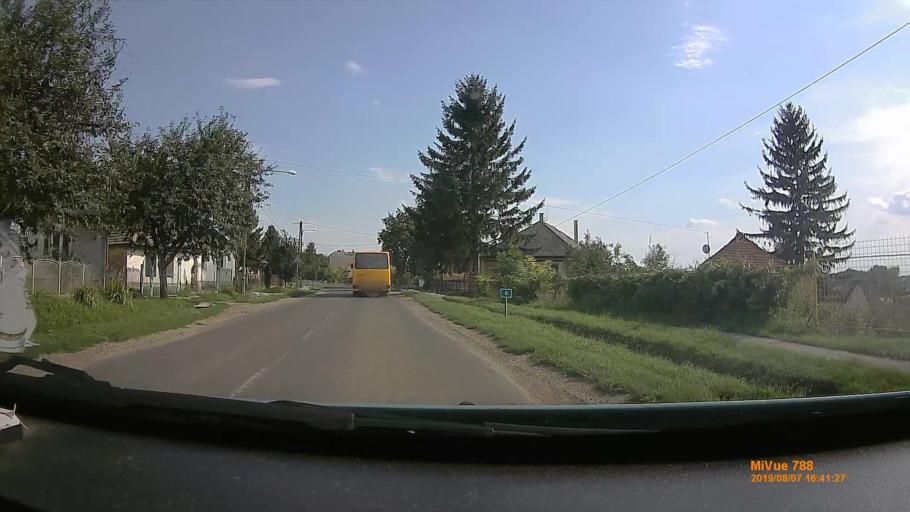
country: HU
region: Borsod-Abauj-Zemplen
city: Encs
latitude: 48.3783
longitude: 21.2134
